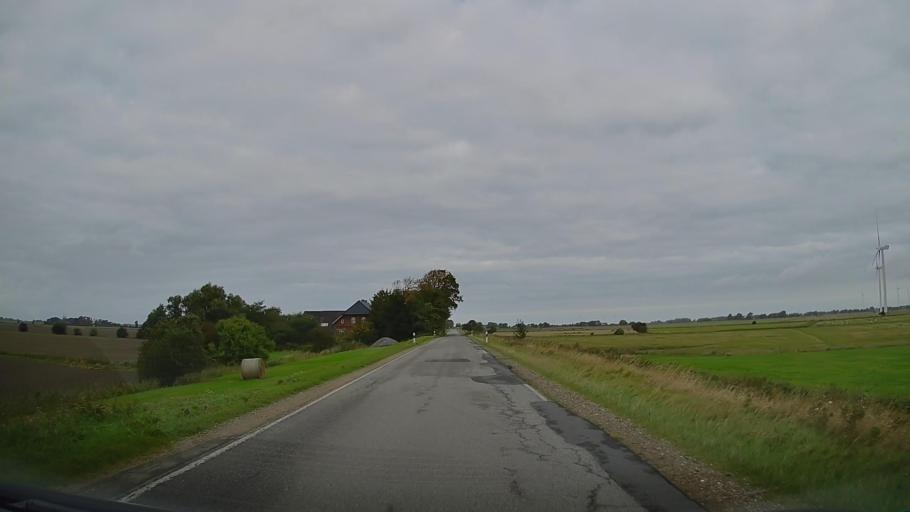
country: DE
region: Schleswig-Holstein
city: Emmelsbull-Horsbull
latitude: 54.7899
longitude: 8.7279
